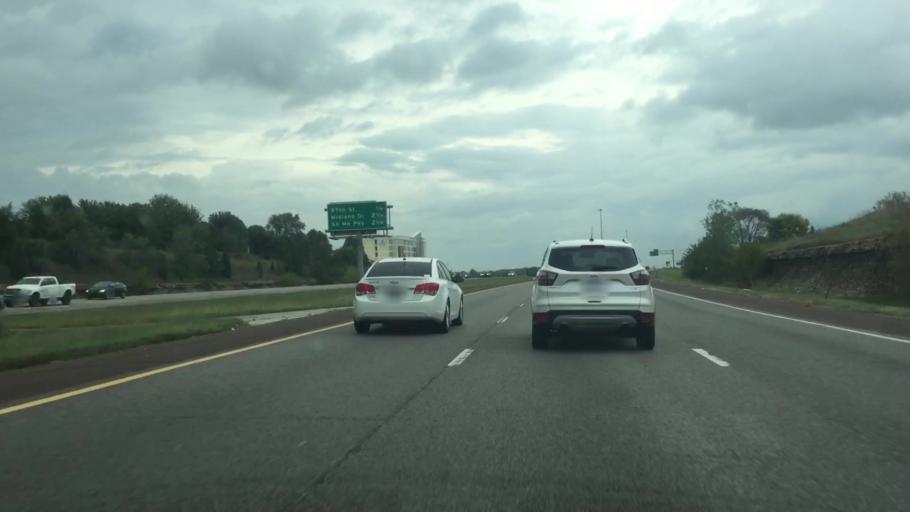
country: US
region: Kansas
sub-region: Johnson County
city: Lenexa
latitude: 38.9648
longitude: -94.7761
